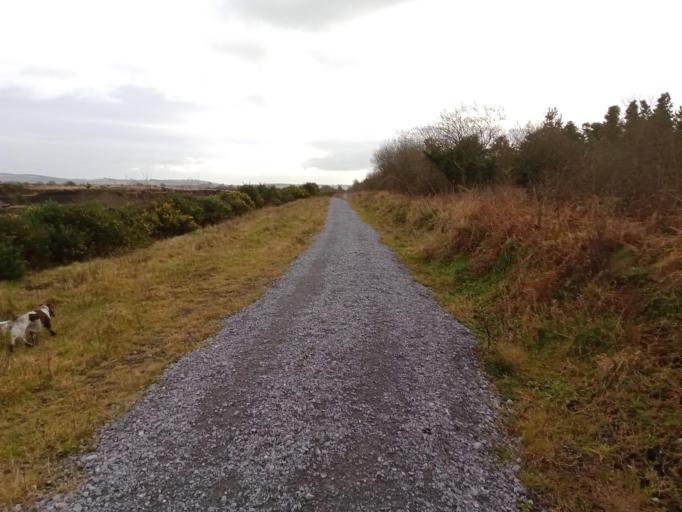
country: IE
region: Munster
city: Thurles
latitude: 52.5982
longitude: -7.7477
